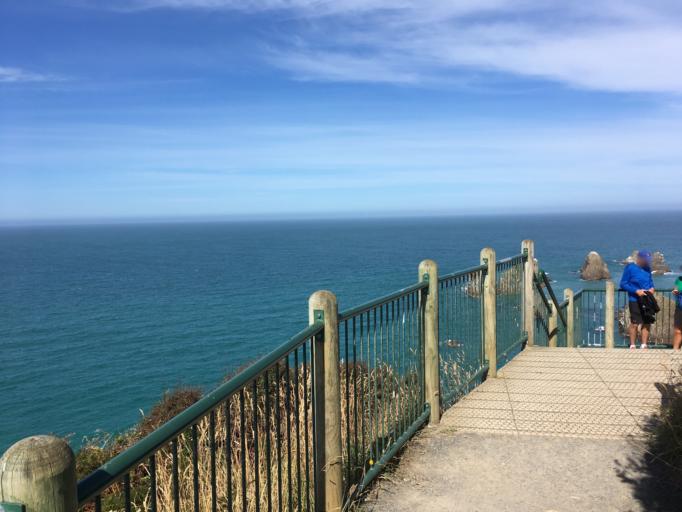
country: NZ
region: Otago
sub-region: Clutha District
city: Balclutha
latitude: -46.4481
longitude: 169.8168
